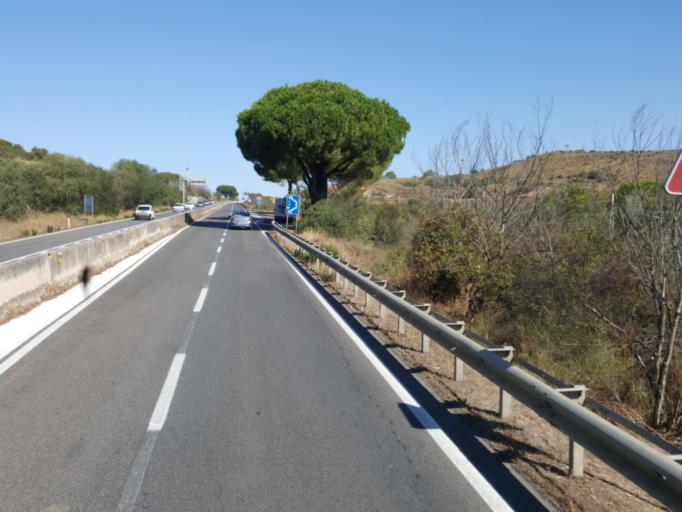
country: IT
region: Tuscany
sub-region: Provincia di Grosseto
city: Fonteblanda
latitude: 42.5528
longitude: 11.1730
